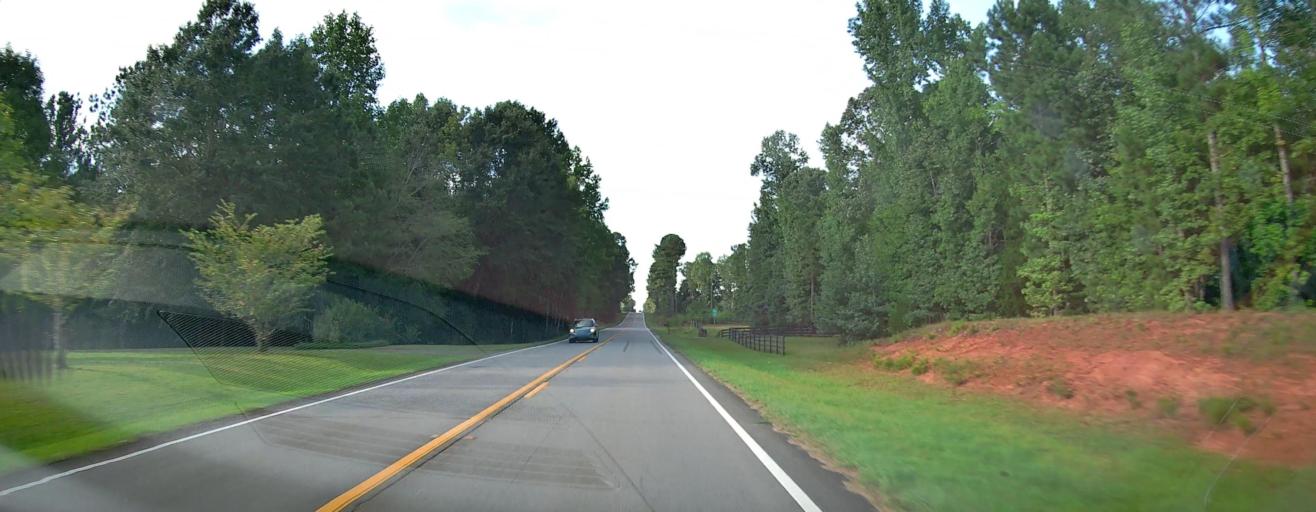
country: US
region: Georgia
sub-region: Monroe County
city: Forsyth
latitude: 32.8886
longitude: -83.9949
